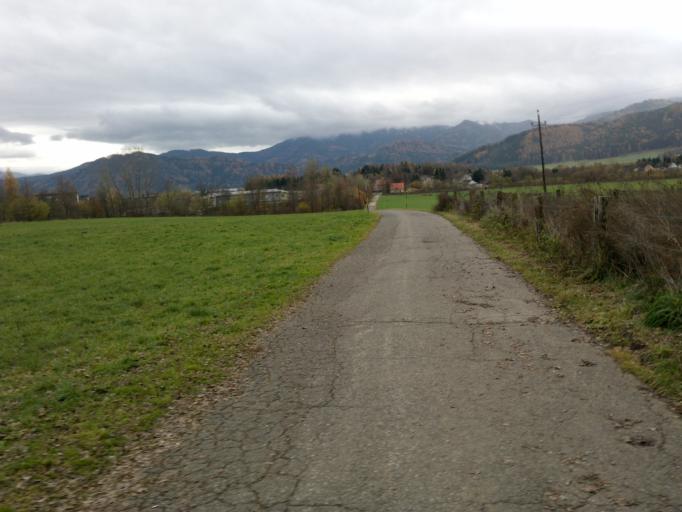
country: AT
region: Styria
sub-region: Politischer Bezirk Murtal
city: Fohnsdorf
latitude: 47.2055
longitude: 14.6600
